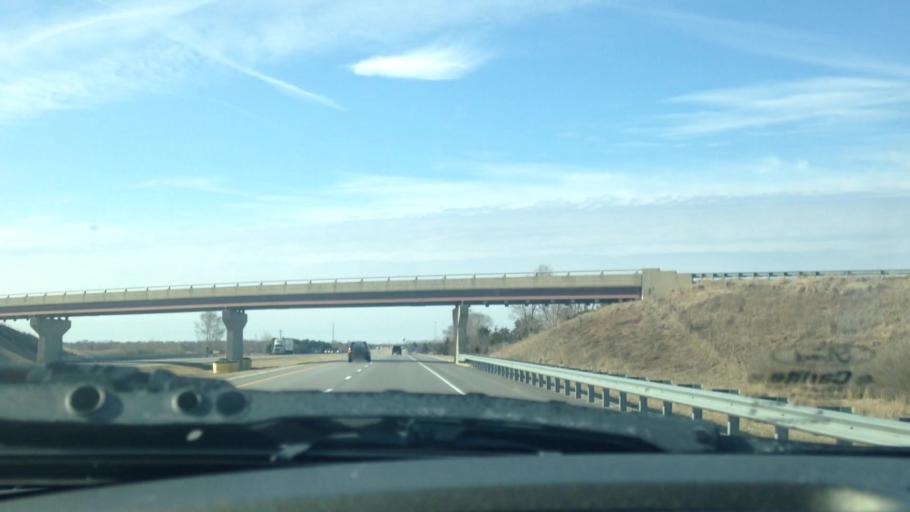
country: US
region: Illinois
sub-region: Ford County
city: Paxton
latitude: 40.4871
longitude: -88.0971
